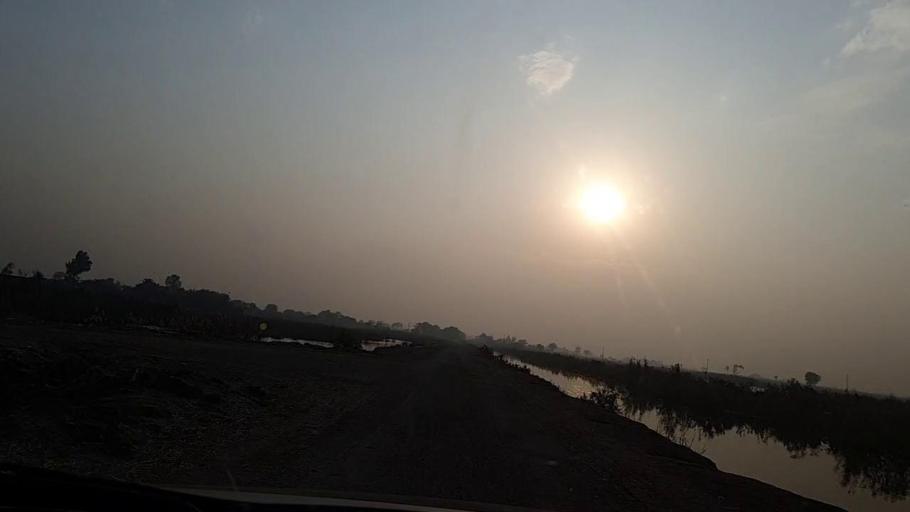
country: PK
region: Sindh
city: Nawabshah
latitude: 26.2971
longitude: 68.2579
